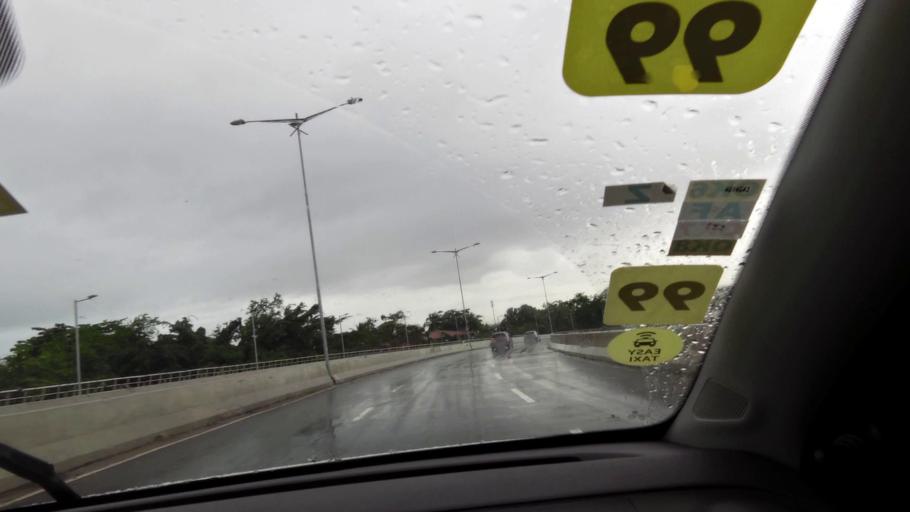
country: BR
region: Pernambuco
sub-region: Recife
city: Recife
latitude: -8.1180
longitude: -34.9010
